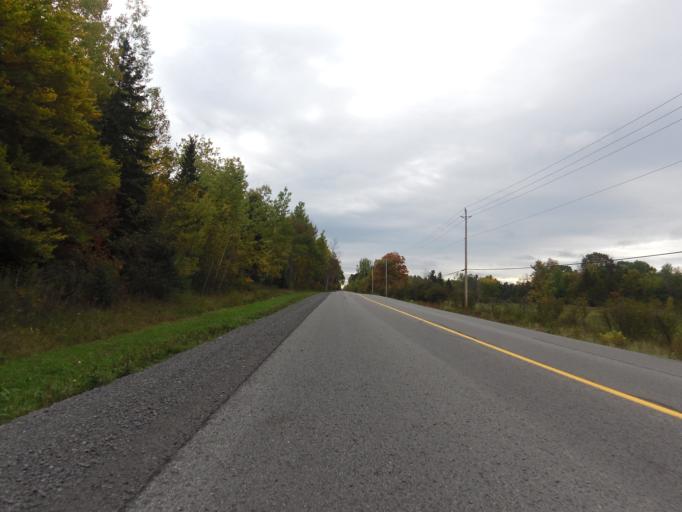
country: CA
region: Ontario
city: Arnprior
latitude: 45.4337
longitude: -76.1109
